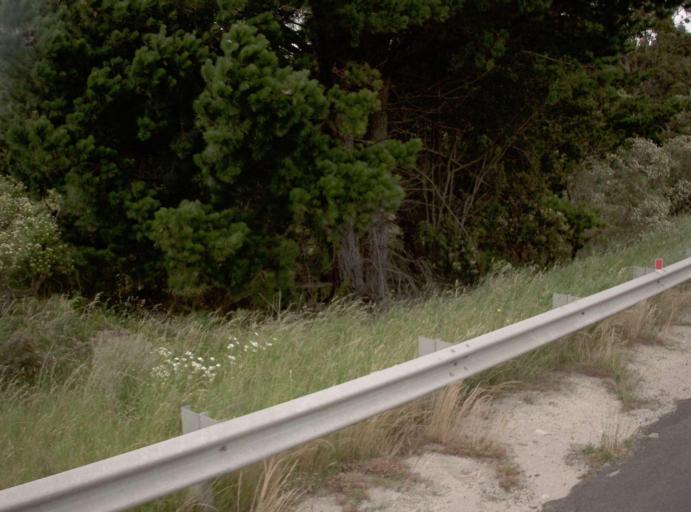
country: AU
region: Victoria
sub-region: Baw Baw
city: Warragul
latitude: -38.4554
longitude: 145.9283
